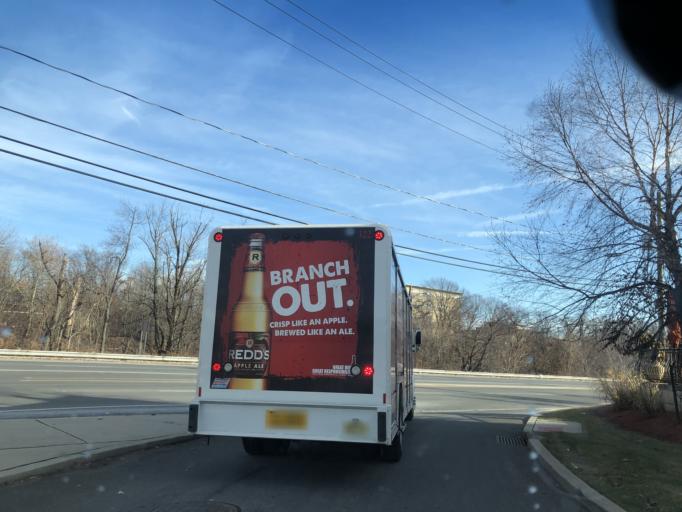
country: US
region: New Jersey
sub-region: Bergen County
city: Fair Lawn
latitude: 40.9364
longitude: -74.1419
